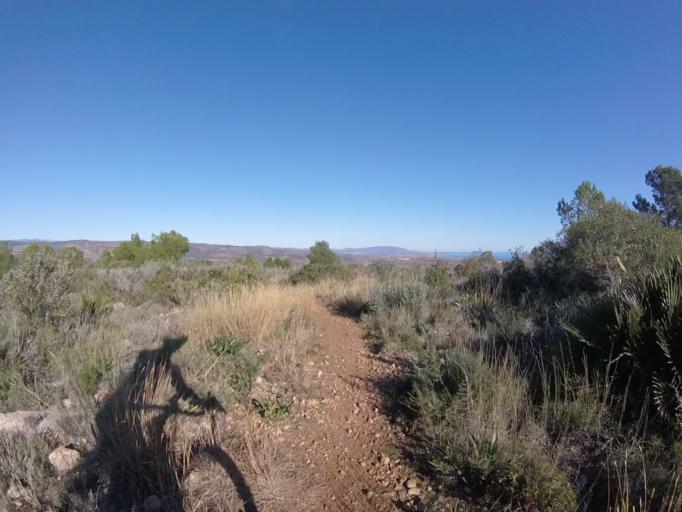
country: ES
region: Valencia
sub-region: Provincia de Castello
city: Orpesa/Oropesa del Mar
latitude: 40.1150
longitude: 0.1164
